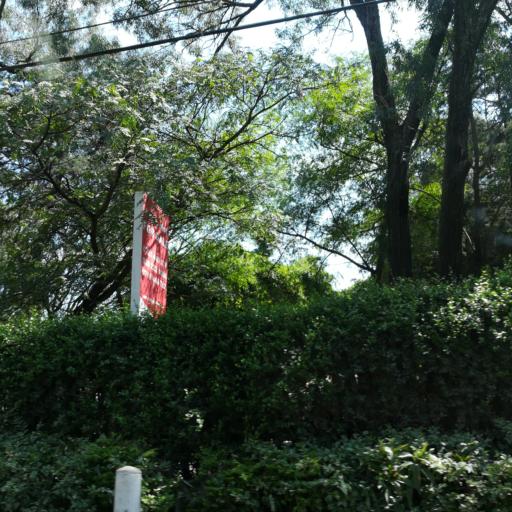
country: KE
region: Nairobi Area
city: Nairobi
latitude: -1.2964
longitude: 36.7900
